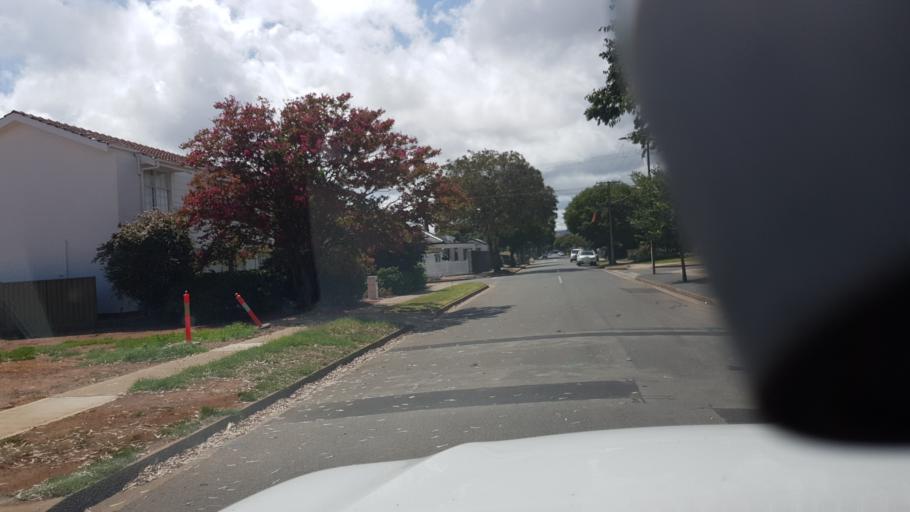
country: AU
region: South Australia
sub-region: Adelaide
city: Brighton
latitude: -35.0169
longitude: 138.5339
